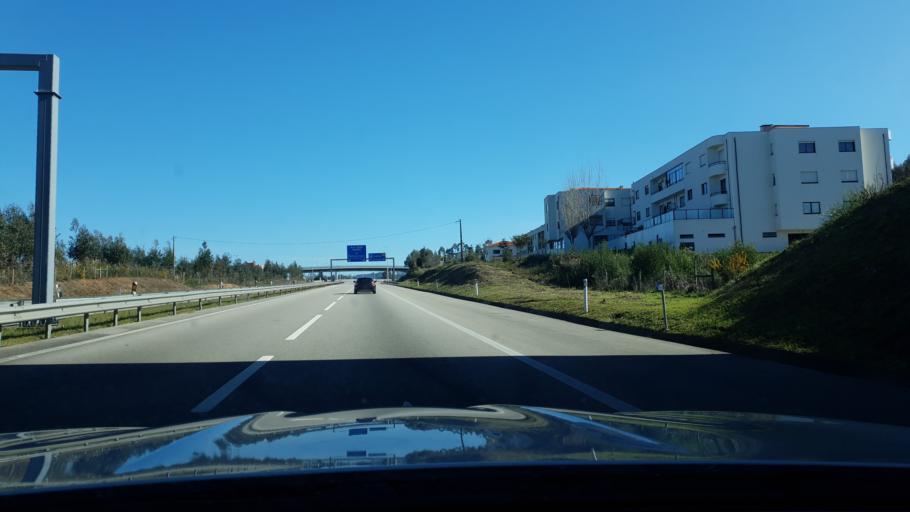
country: PT
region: Aveiro
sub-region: Santa Maria da Feira
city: Nogueira da Regedoura
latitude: 41.0102
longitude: -8.5926
